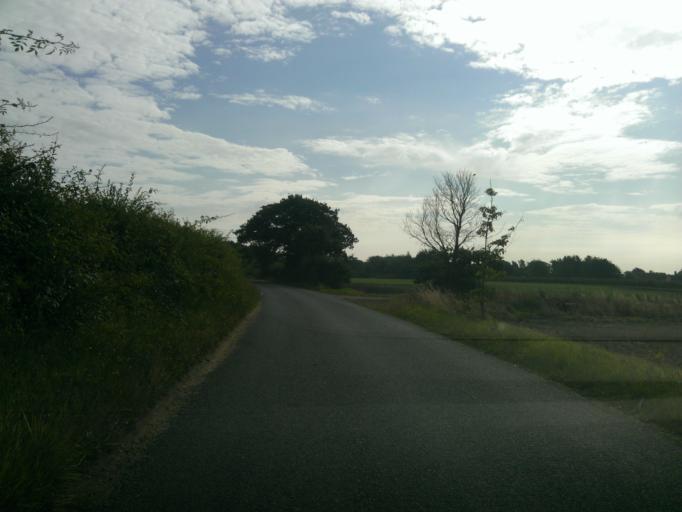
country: GB
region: England
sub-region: Essex
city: Great Bentley
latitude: 51.8336
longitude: 1.0685
